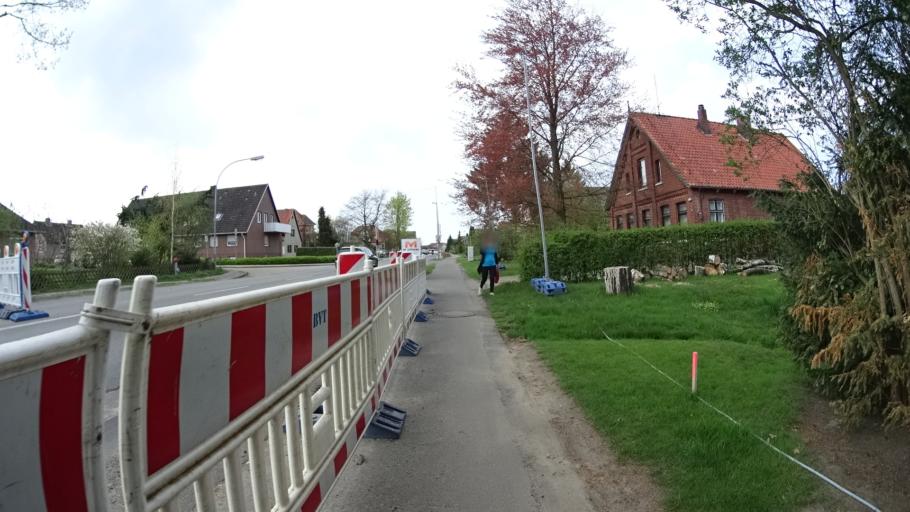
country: DE
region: Lower Saxony
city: Jork
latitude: 53.5275
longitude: 9.7028
